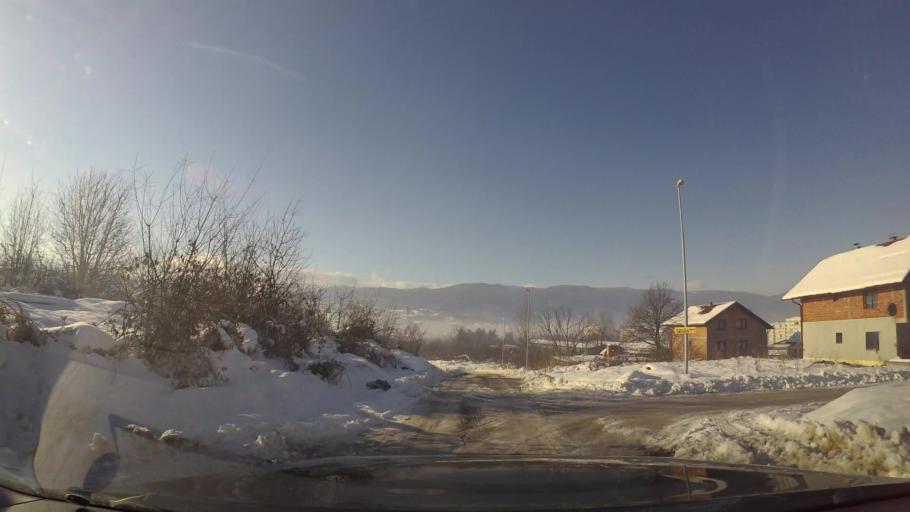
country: BA
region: Federation of Bosnia and Herzegovina
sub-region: Kanton Sarajevo
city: Sarajevo
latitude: 43.8196
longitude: 18.3697
